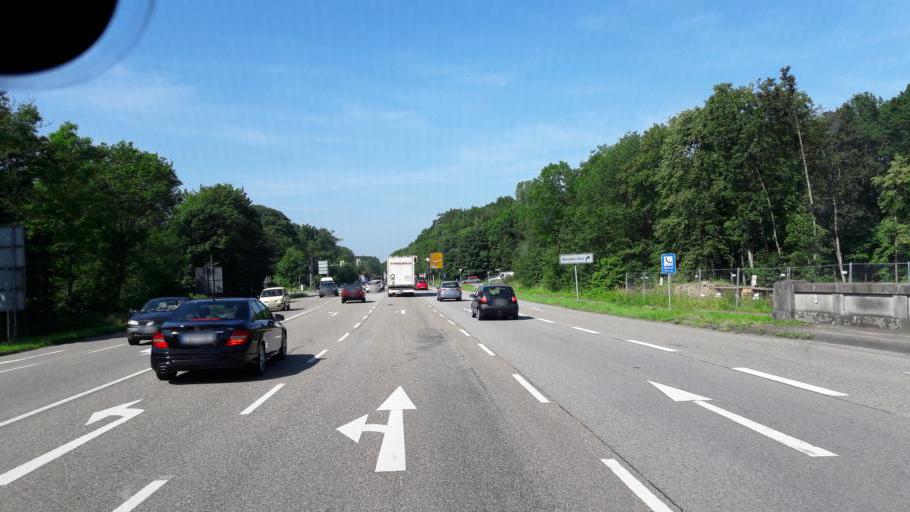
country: DE
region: Baden-Wuerttemberg
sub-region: Karlsruhe Region
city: Otigheim
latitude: 48.8711
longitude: 8.2349
